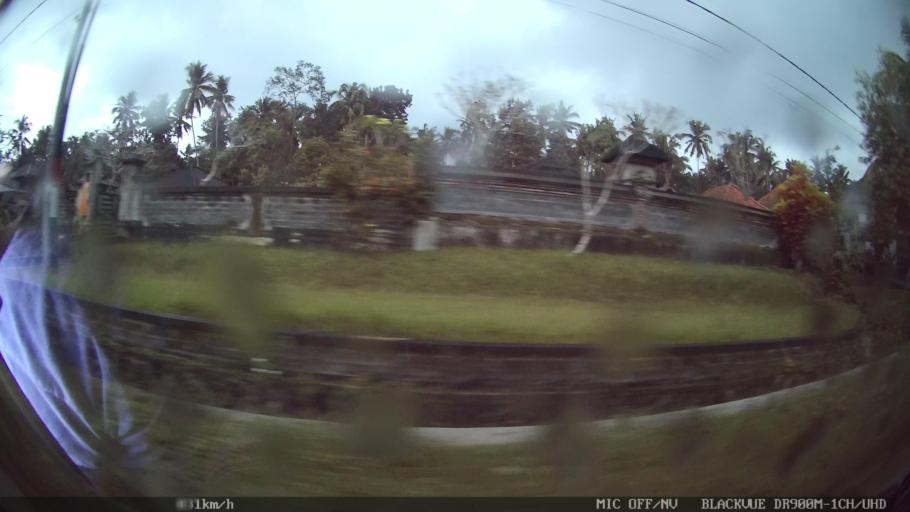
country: ID
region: Bali
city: Banjar Tengah
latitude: -8.4920
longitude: 115.1883
